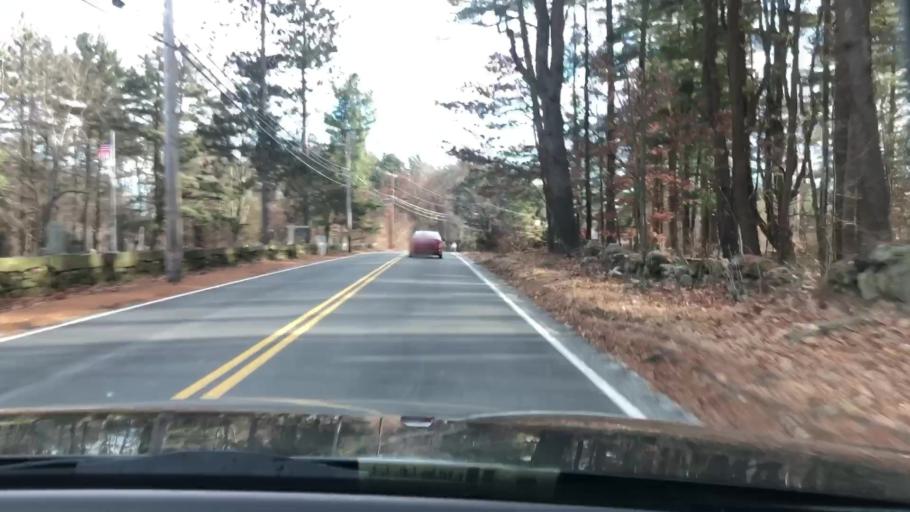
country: US
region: Massachusetts
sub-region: Worcester County
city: Milford
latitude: 42.1116
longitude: -71.5143
